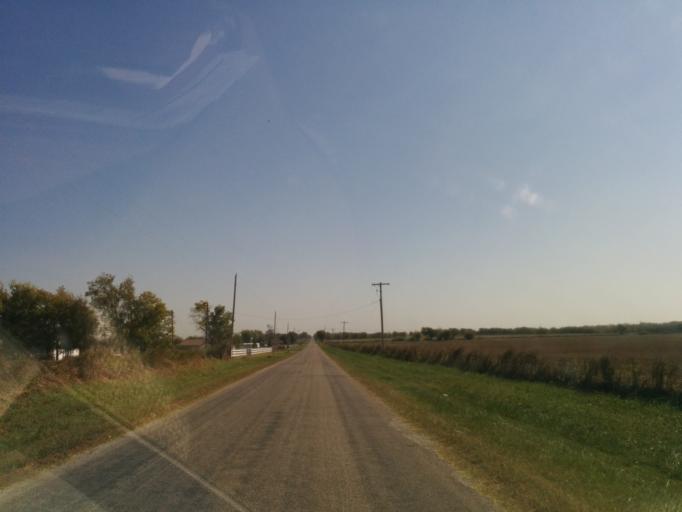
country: US
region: Oklahoma
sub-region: Okmulgee County
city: Beggs
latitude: 35.7990
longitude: -96.0742
